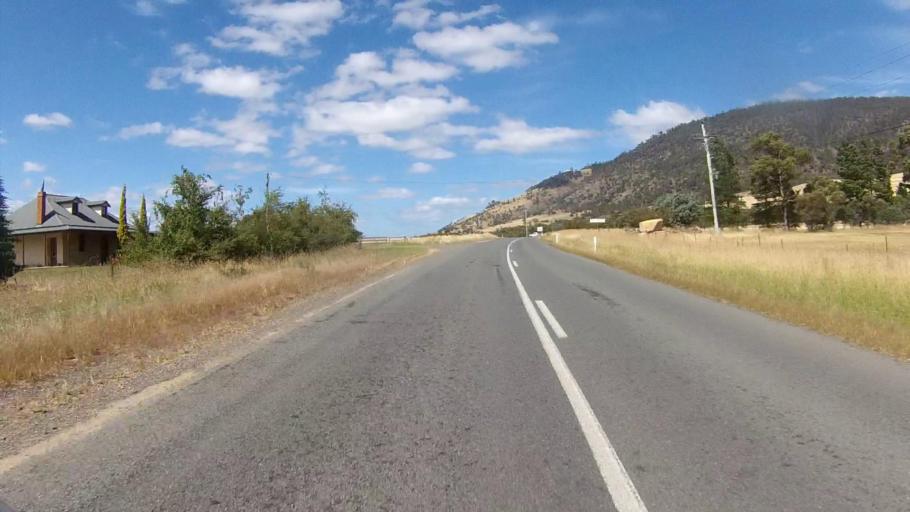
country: AU
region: Tasmania
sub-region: Sorell
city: Sorell
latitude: -42.6224
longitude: 147.4295
